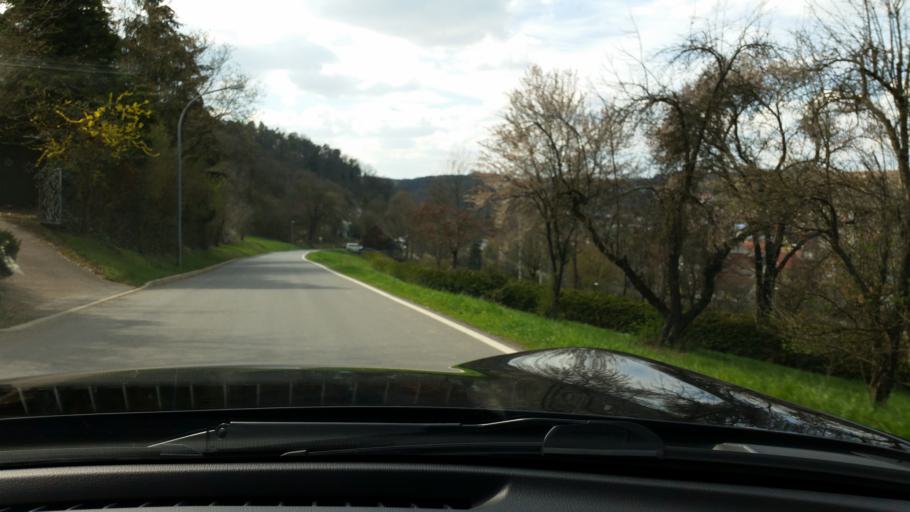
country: DE
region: Baden-Wuerttemberg
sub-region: Karlsruhe Region
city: Adelsheim
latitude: 49.3786
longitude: 9.3872
